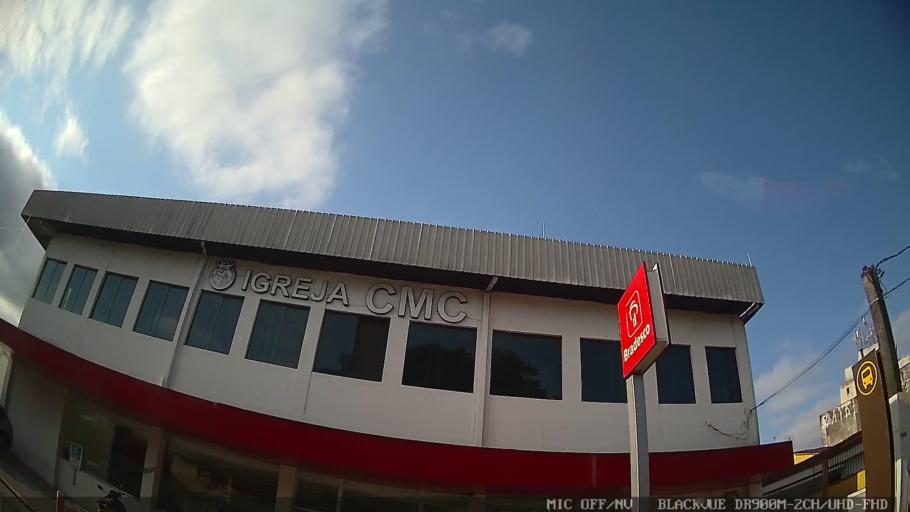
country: BR
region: Sao Paulo
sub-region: Taboao Da Serra
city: Taboao da Serra
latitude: -23.6337
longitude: -46.7726
